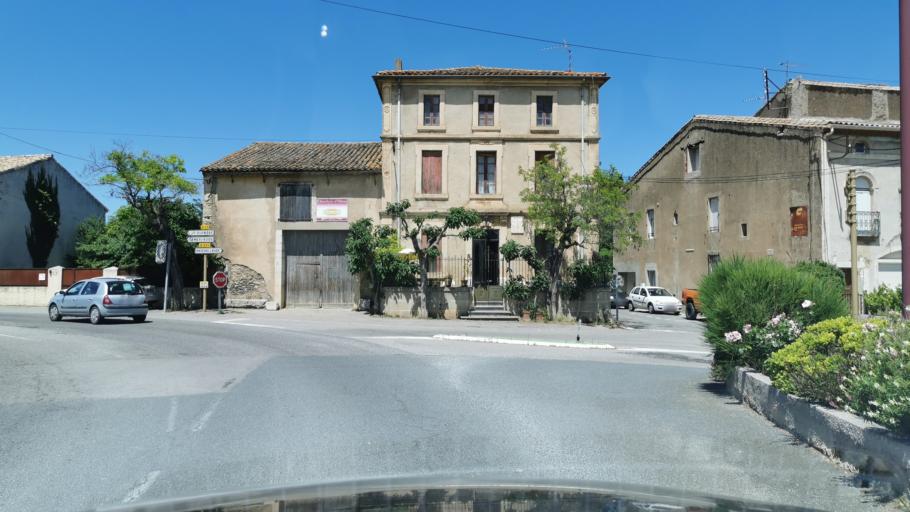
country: FR
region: Languedoc-Roussillon
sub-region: Departement de l'Aude
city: Canet
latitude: 43.2153
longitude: 2.8629
